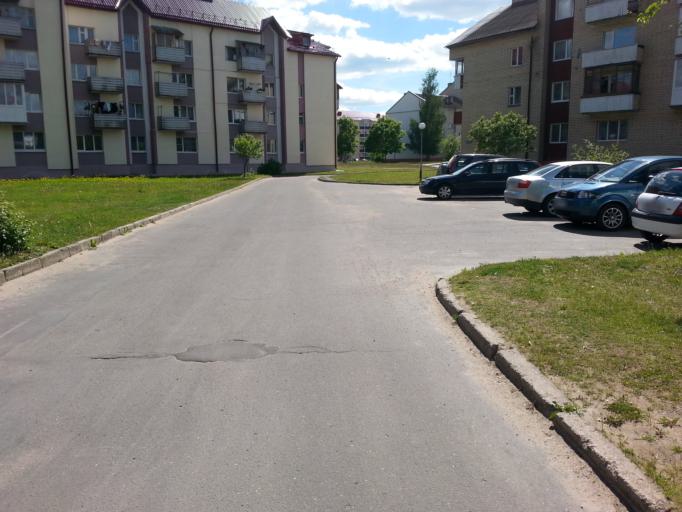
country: BY
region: Minsk
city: Narach
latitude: 54.9160
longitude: 26.7022
